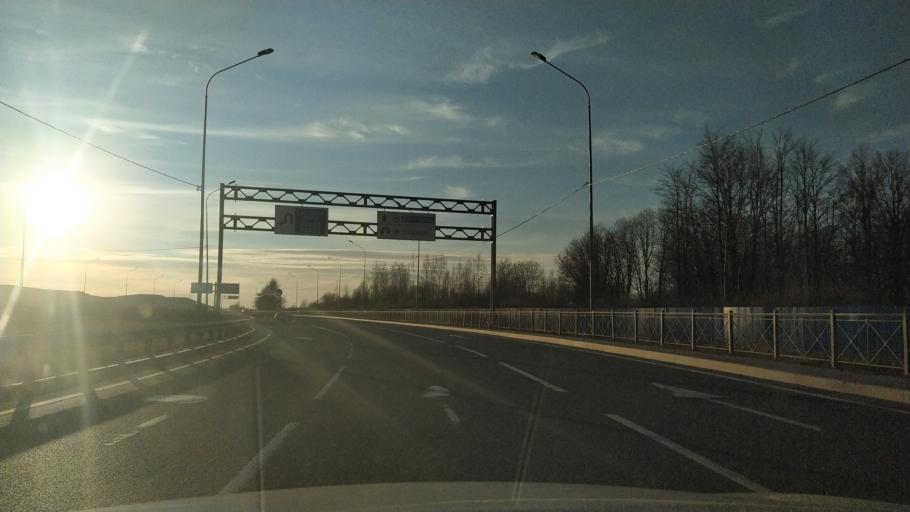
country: RU
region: St.-Petersburg
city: Aleksandrovskaya
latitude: 59.7474
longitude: 30.3025
